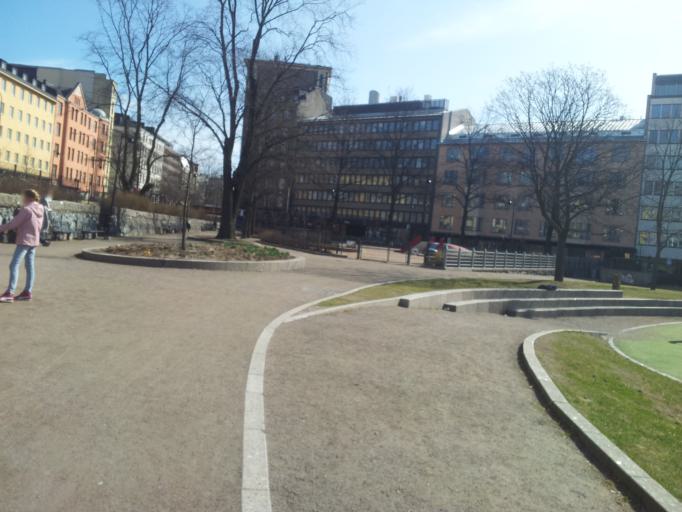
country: FI
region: Uusimaa
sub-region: Helsinki
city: Helsinki
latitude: 60.1670
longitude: 24.9281
